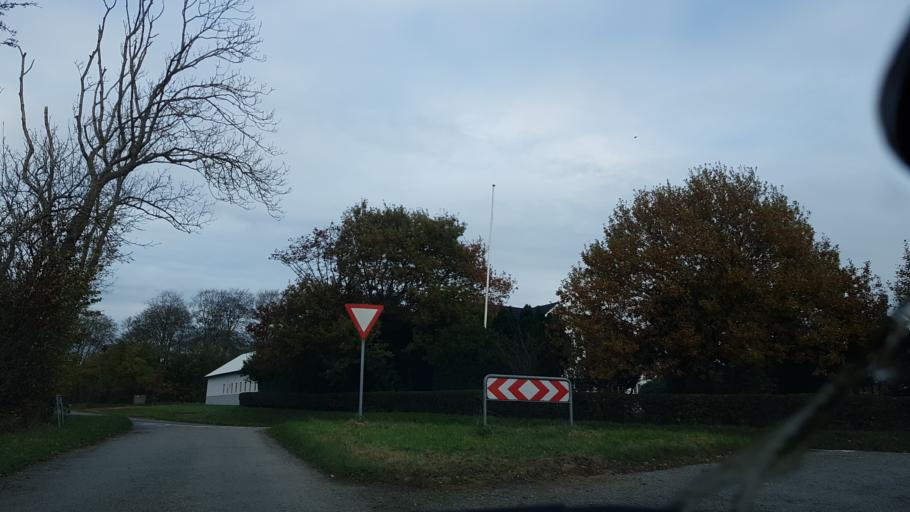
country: DK
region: South Denmark
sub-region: Haderslev Kommune
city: Vojens
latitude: 55.2528
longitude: 9.1918
